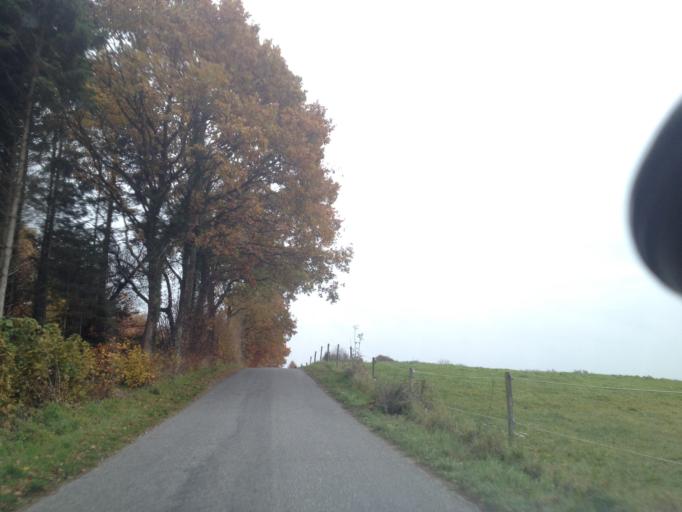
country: DK
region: South Denmark
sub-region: Assens Kommune
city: Vissenbjerg
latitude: 55.4260
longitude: 10.2041
